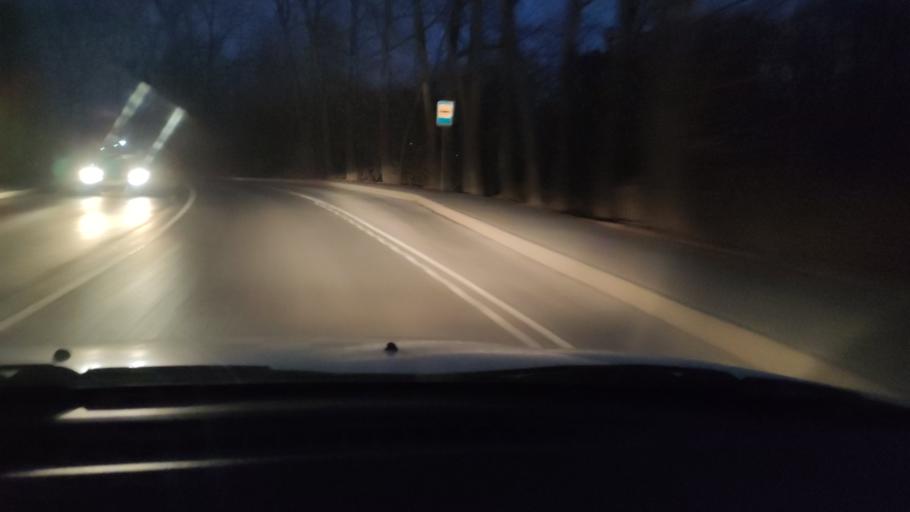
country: RU
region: Perm
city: Perm
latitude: 57.9607
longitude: 56.2062
